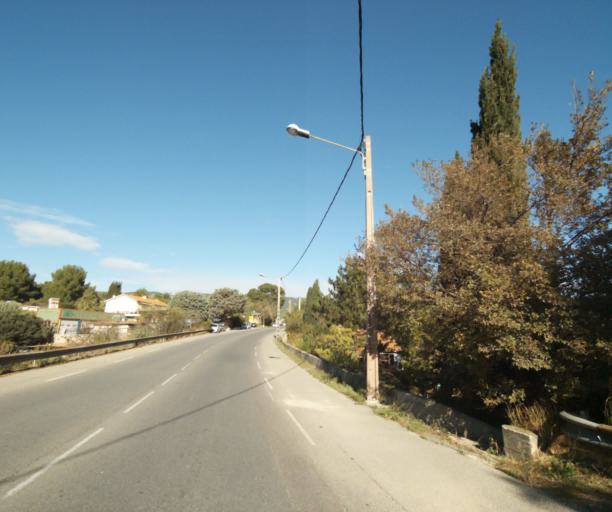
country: FR
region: Provence-Alpes-Cote d'Azur
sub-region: Departement des Bouches-du-Rhone
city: Ceyreste
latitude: 43.2049
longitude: 5.6267
